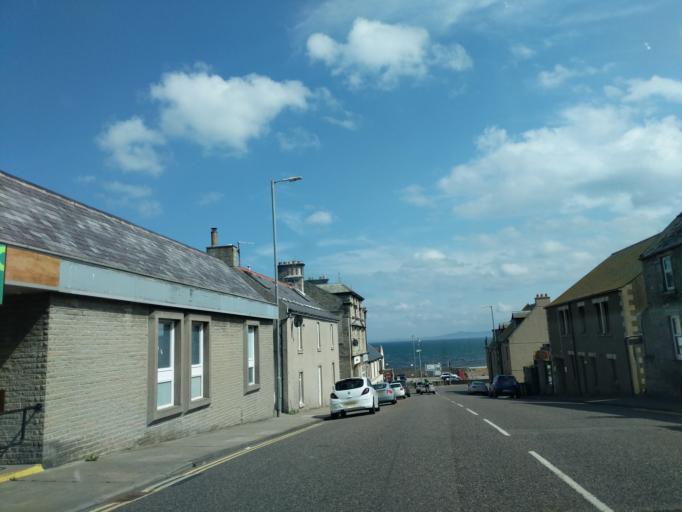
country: GB
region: Scotland
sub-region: Moray
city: Lossiemouth
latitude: 57.7222
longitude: -3.2815
